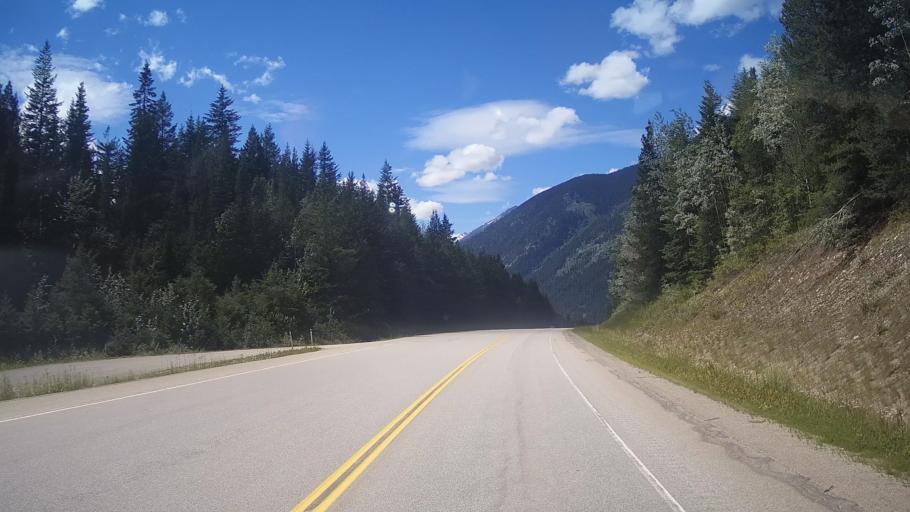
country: CA
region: Alberta
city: Grande Cache
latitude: 53.0316
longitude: -119.2086
